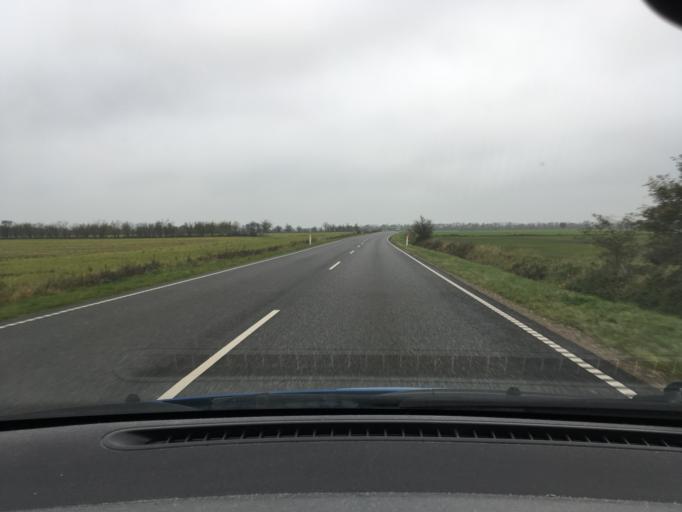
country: DK
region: South Denmark
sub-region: Tonder Kommune
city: Toftlund
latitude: 55.0559
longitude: 9.1148
